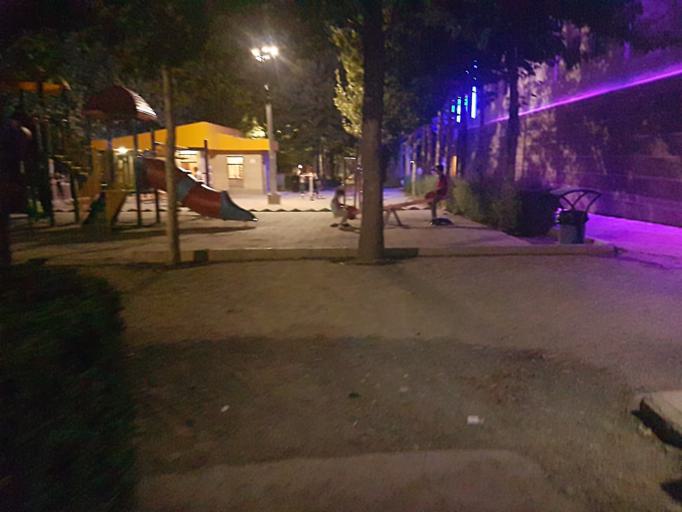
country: IR
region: Markazi
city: Arak
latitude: 34.0666
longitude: 49.6795
